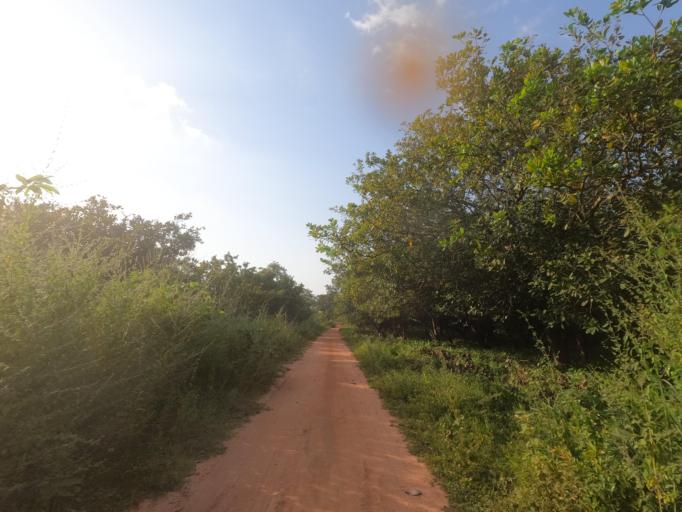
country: GW
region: Oio
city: Bissora
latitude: 12.3454
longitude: -15.6854
